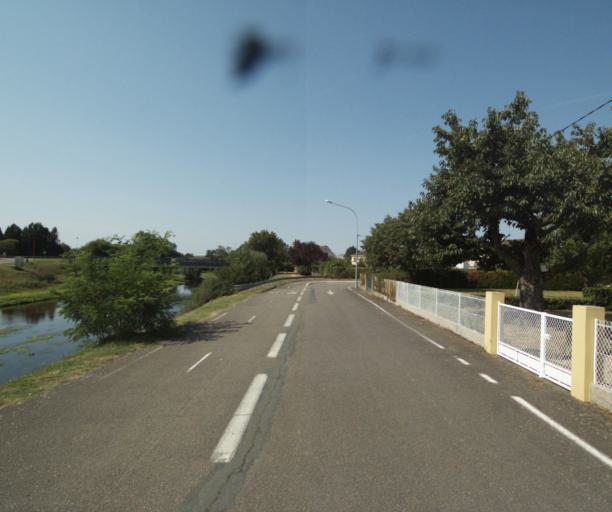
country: FR
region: Bourgogne
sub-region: Departement de Saone-et-Loire
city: Gueugnon
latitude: 46.5966
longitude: 4.0538
